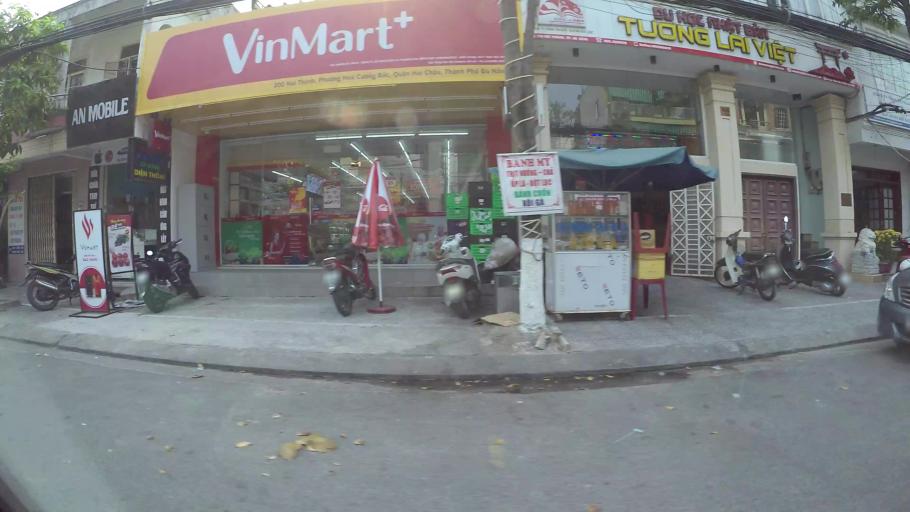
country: VN
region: Da Nang
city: Son Tra
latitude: 16.0450
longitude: 108.2212
